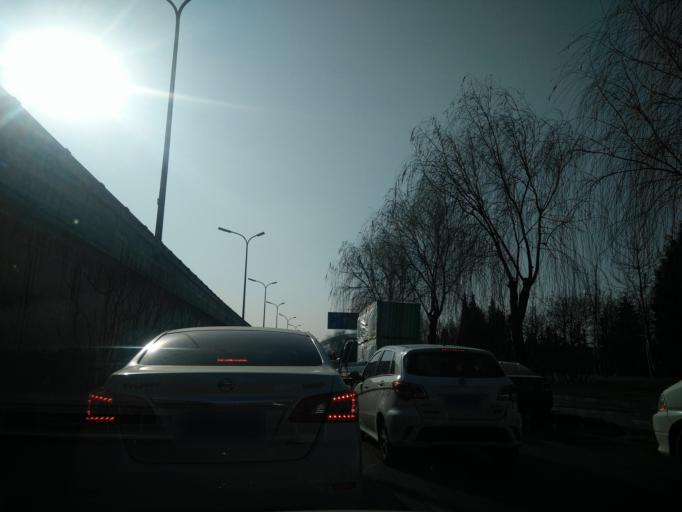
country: CN
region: Beijing
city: Jiugong
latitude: 39.8488
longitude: 116.4790
